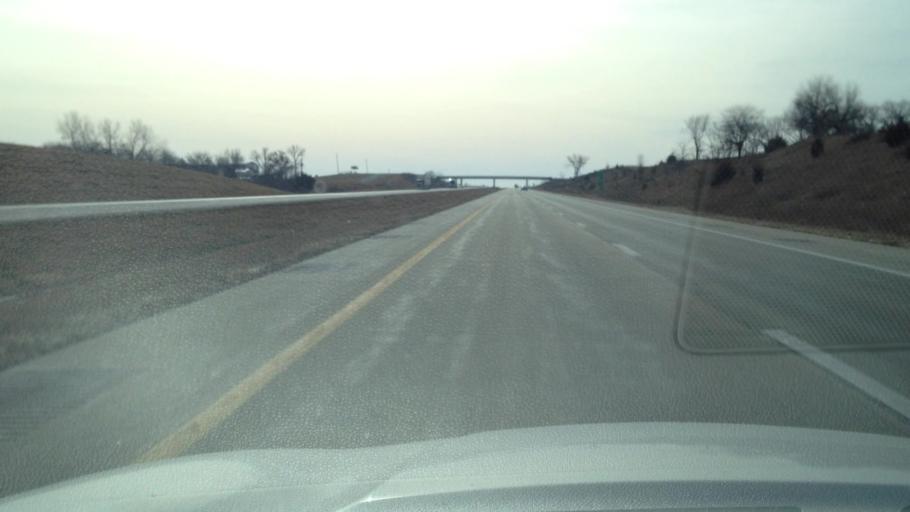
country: US
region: Missouri
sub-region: Harrison County
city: Bethany
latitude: 40.3182
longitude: -94.0118
